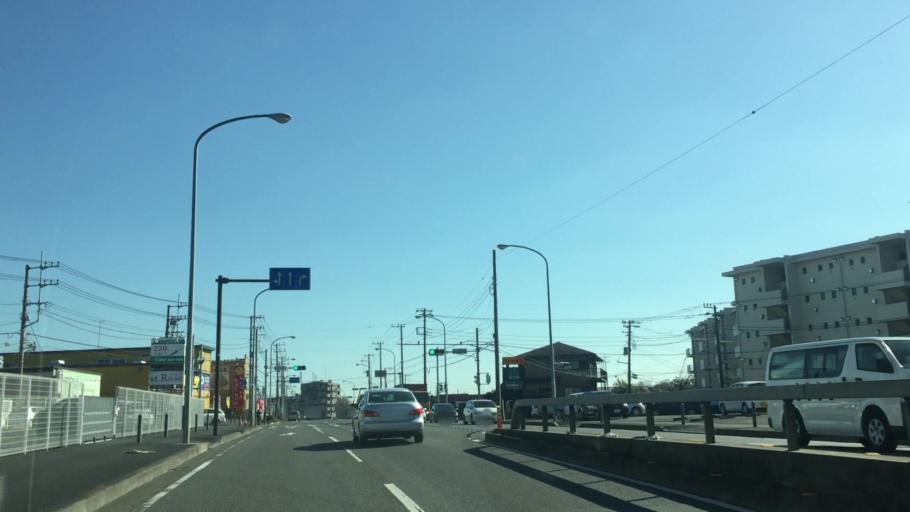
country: JP
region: Kanagawa
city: Yokohama
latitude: 35.4837
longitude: 139.5965
